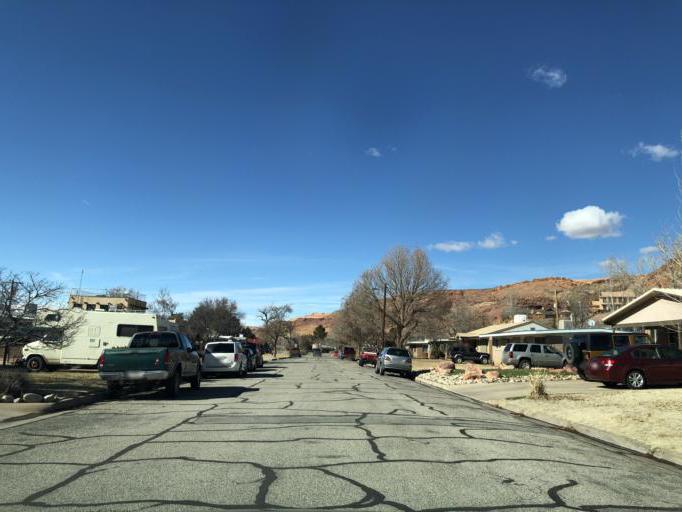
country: US
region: Utah
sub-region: Grand County
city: Moab
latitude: 38.5688
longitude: -109.5365
